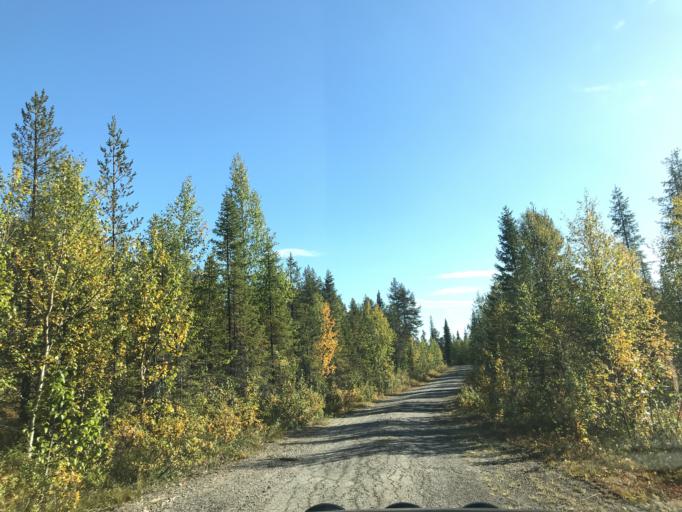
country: SE
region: Norrbotten
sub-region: Gallivare Kommun
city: Malmberget
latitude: 67.6472
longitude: 21.0855
